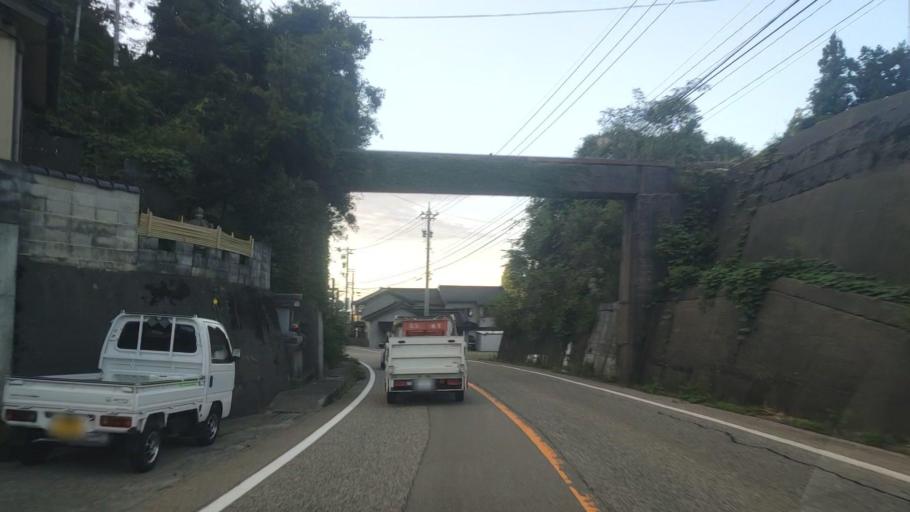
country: JP
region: Toyama
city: Nanto-shi
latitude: 36.5682
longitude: 136.9930
